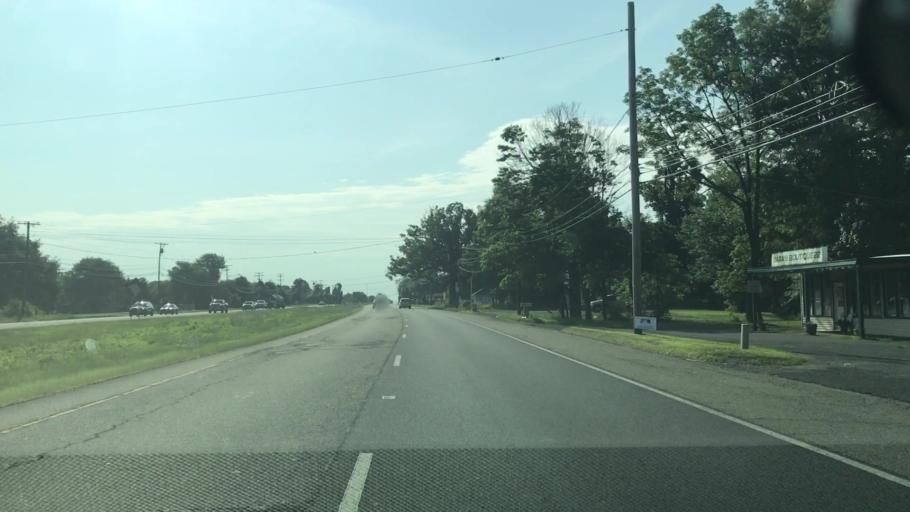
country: US
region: New Jersey
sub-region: Somerset County
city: Bridgewater
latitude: 40.6081
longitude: -74.7080
